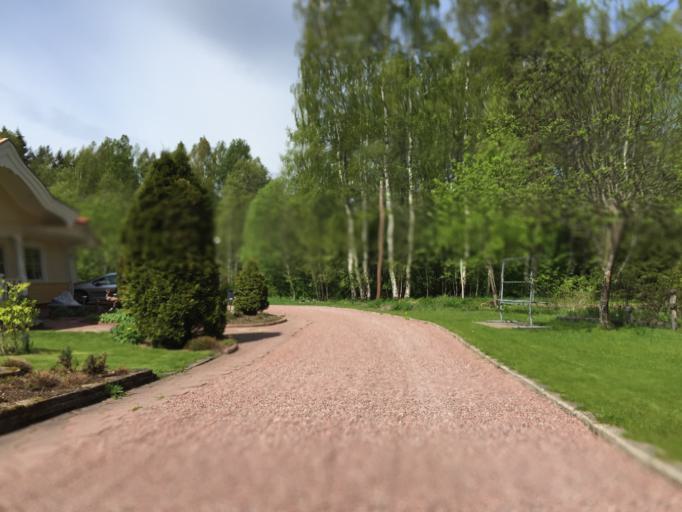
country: SE
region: Dalarna
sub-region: Ludvika Kommun
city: Ludvika
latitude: 60.1368
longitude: 15.1492
